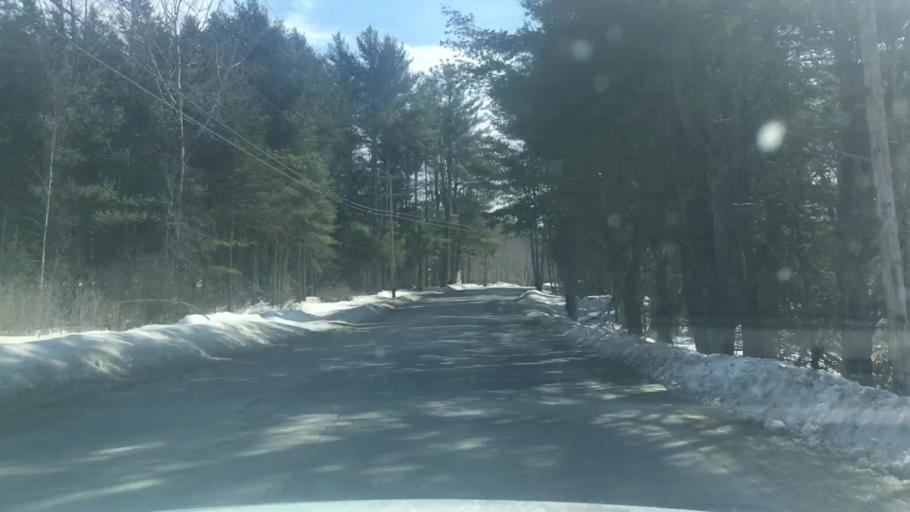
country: US
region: Maine
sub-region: Penobscot County
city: Holden
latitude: 44.7535
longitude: -68.6345
